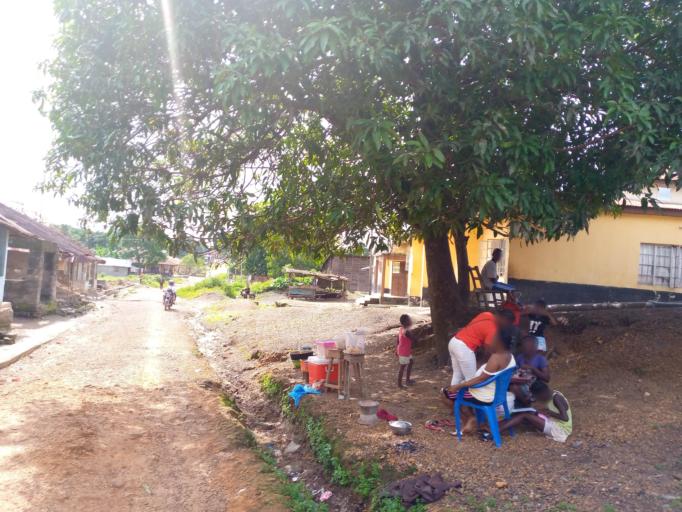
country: SL
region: Northern Province
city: Magburaka
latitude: 8.7230
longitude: -11.9461
